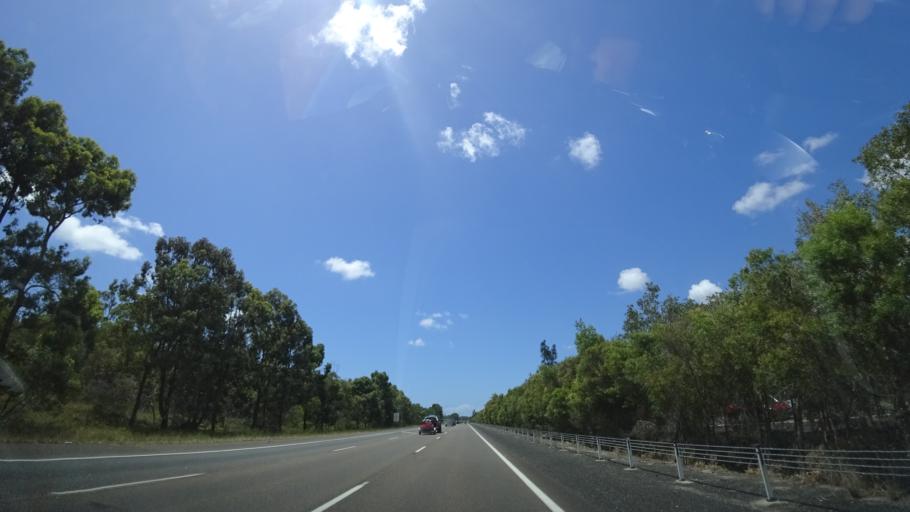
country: AU
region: Queensland
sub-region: Sunshine Coast
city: Mooloolaba
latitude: -26.6850
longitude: 153.1047
